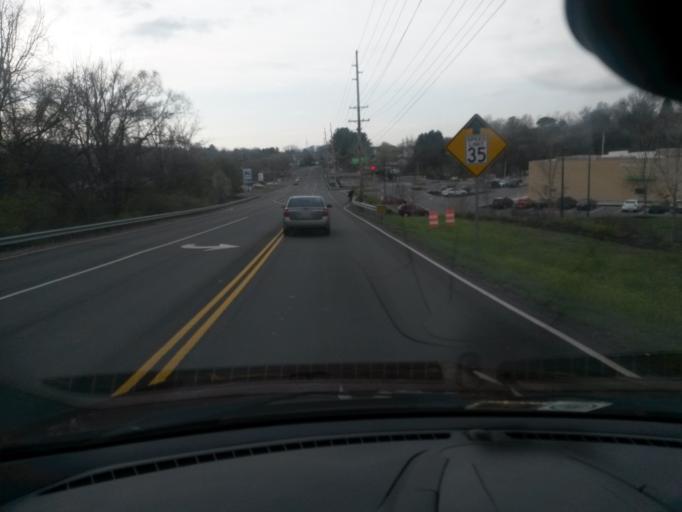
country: US
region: Virginia
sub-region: Roanoke County
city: Hollins
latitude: 37.3237
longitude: -79.9360
